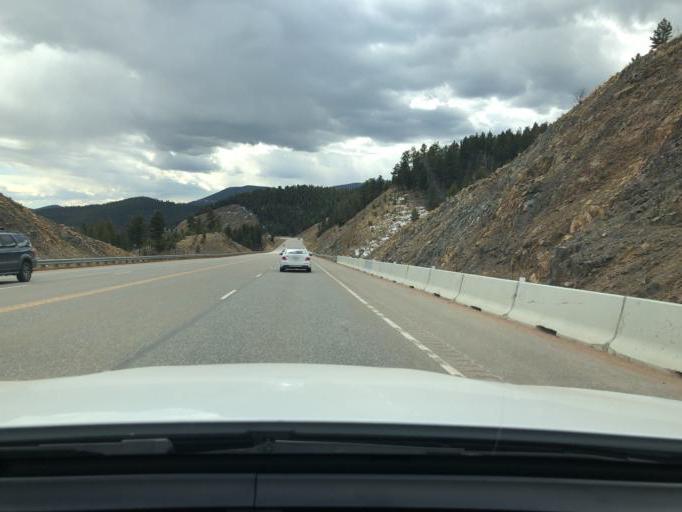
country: US
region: Colorado
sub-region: Gilpin County
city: Central City
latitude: 39.7745
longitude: -105.4733
